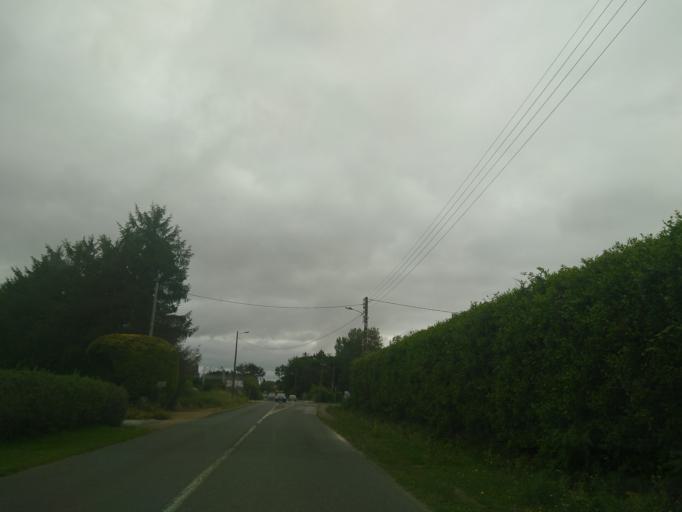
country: FR
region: Brittany
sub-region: Departement du Finistere
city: Plomodiern
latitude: 48.1695
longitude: -4.2798
